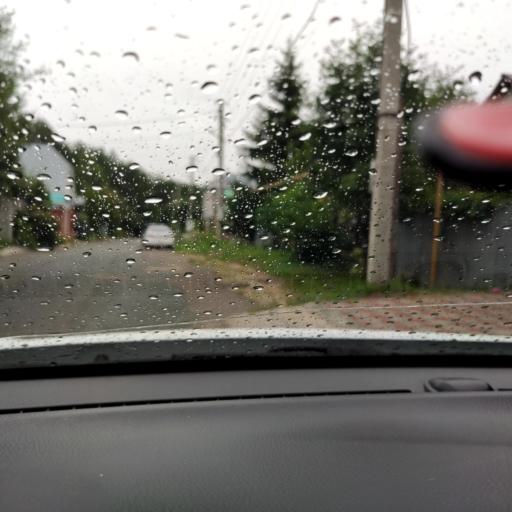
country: RU
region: Tatarstan
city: Vysokaya Gora
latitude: 55.8472
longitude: 49.2391
